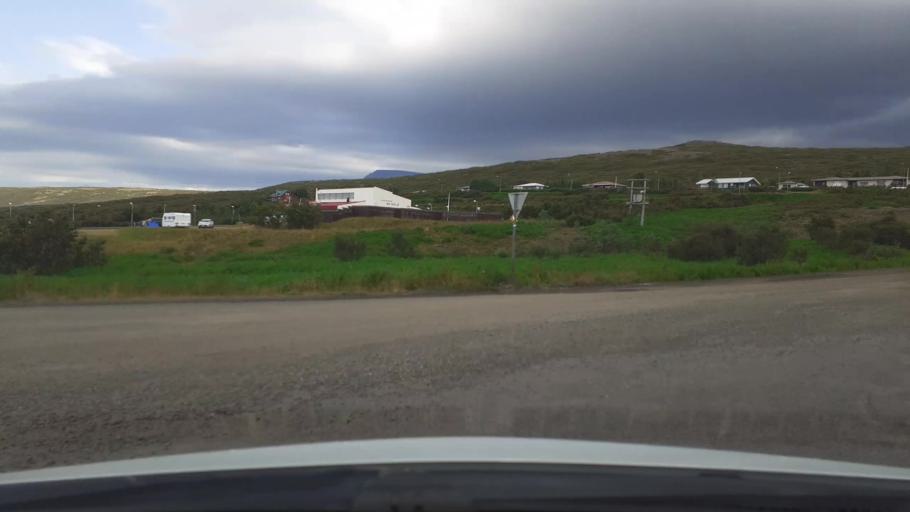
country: IS
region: Capital Region
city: Mosfellsbaer
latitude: 64.4101
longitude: -21.6063
